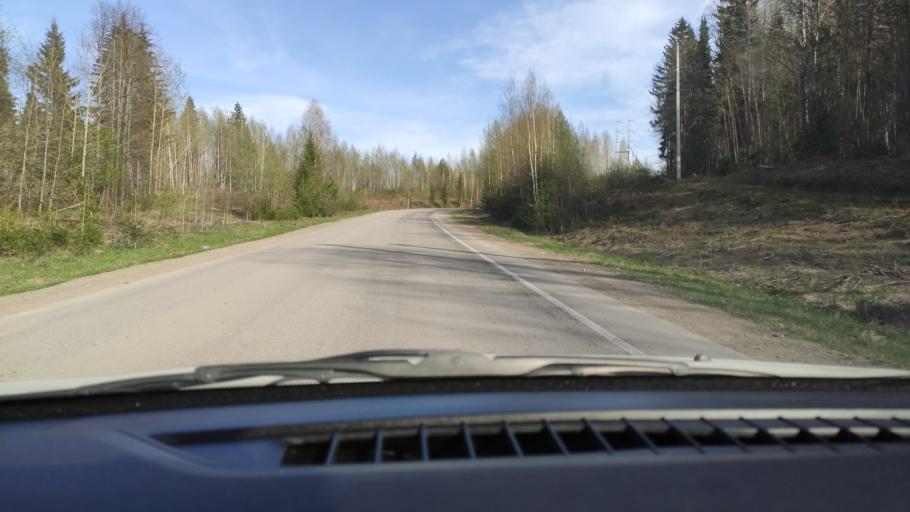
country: RU
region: Perm
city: Novyye Lyady
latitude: 57.9287
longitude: 56.6495
